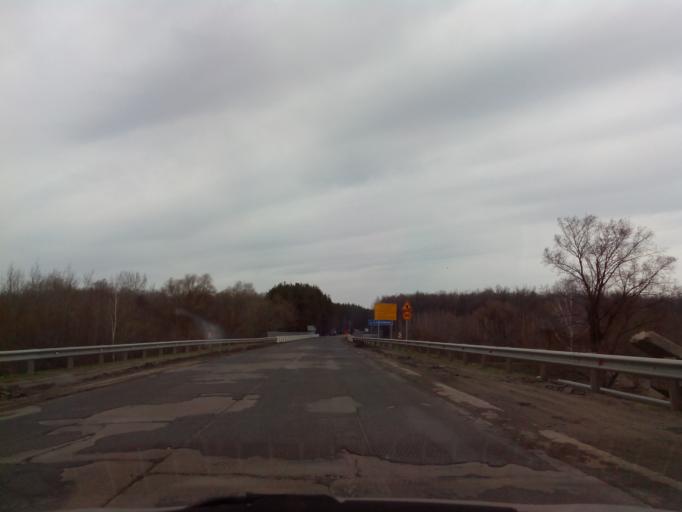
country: RU
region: Tambov
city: Znamenka
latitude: 52.5308
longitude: 41.3572
